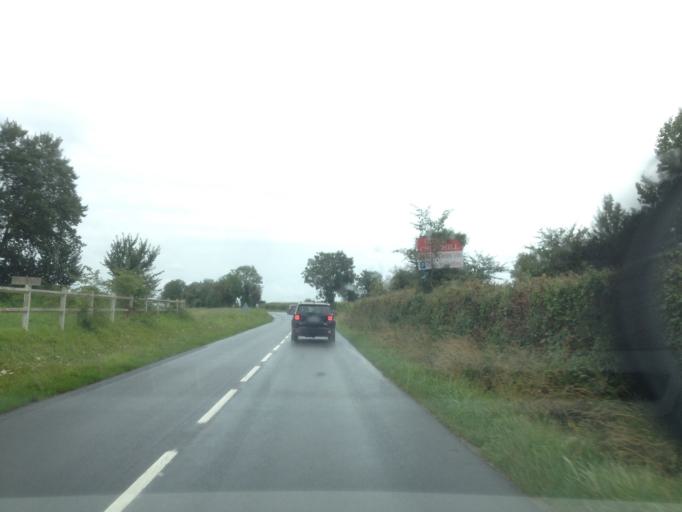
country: FR
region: Lower Normandy
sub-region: Departement du Calvados
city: Saint-Vigor-le-Grand
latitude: 49.3019
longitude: -0.6835
